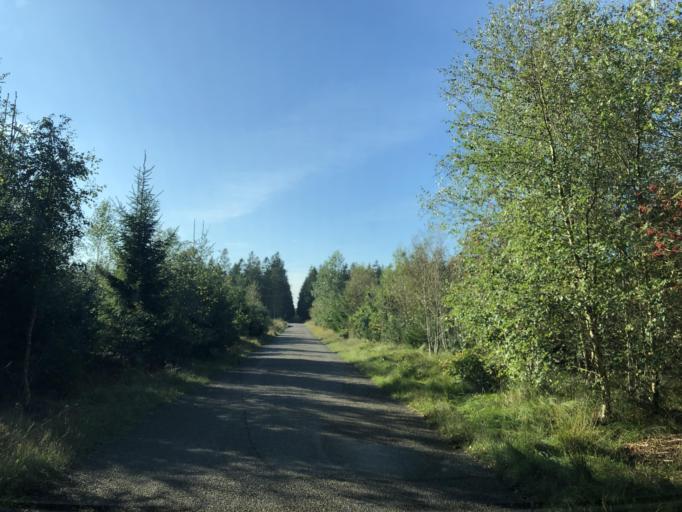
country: DK
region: Central Jutland
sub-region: Holstebro Kommune
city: Holstebro
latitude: 56.3191
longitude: 8.5087
